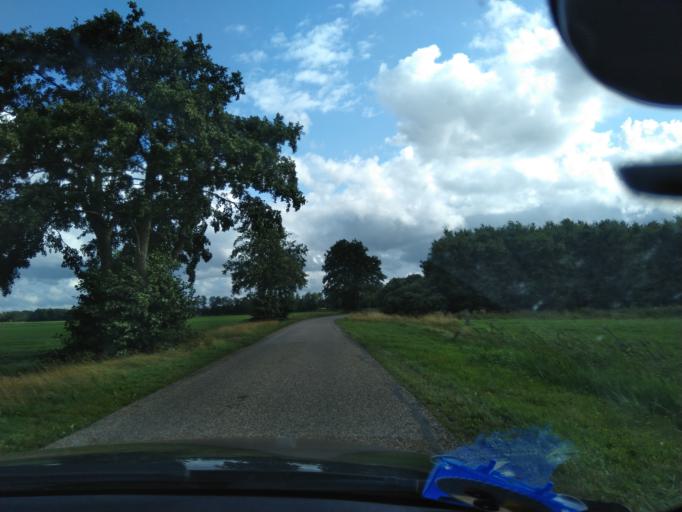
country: NL
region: Drenthe
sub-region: Gemeente Tynaarlo
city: Vries
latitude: 53.0647
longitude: 6.5462
